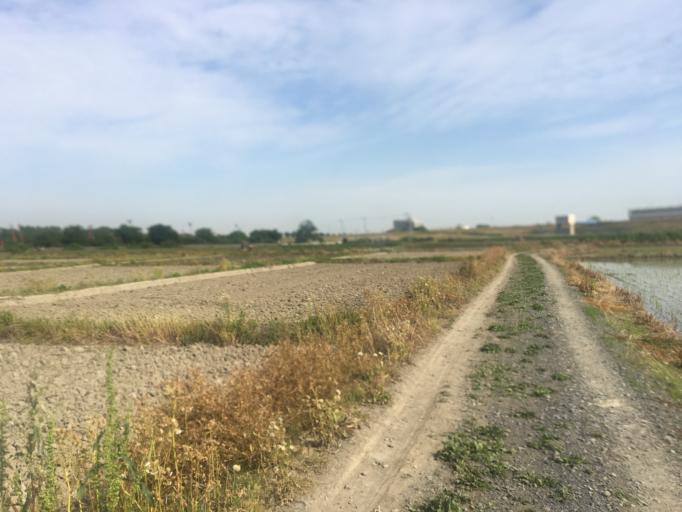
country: JP
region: Saitama
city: Shiki
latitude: 35.8533
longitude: 139.6050
